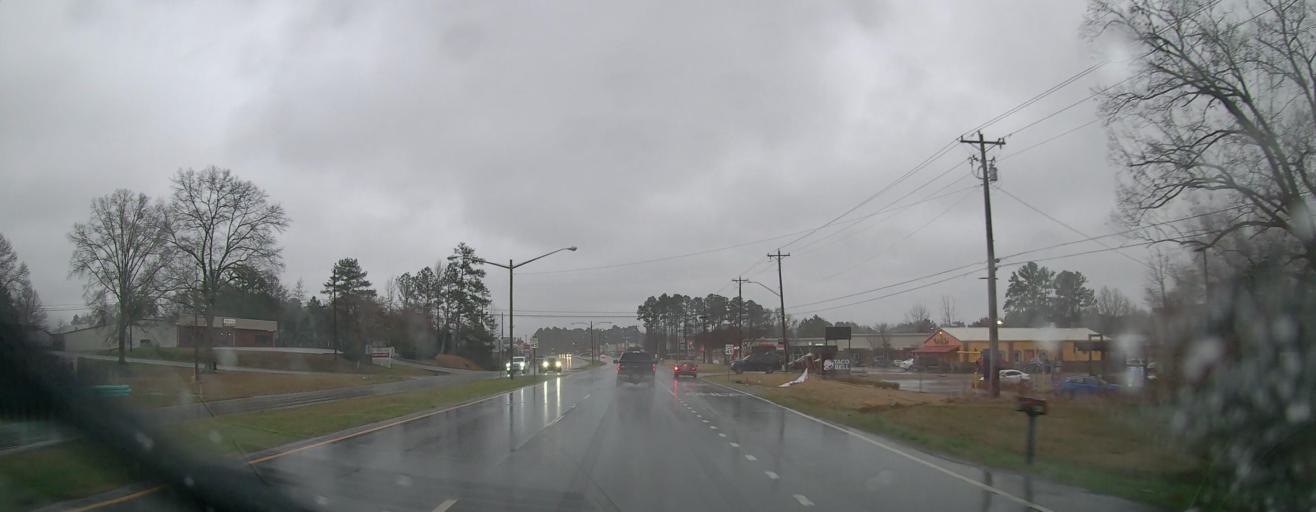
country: US
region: Alabama
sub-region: Morgan County
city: Hartselle
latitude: 34.4566
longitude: -86.9471
